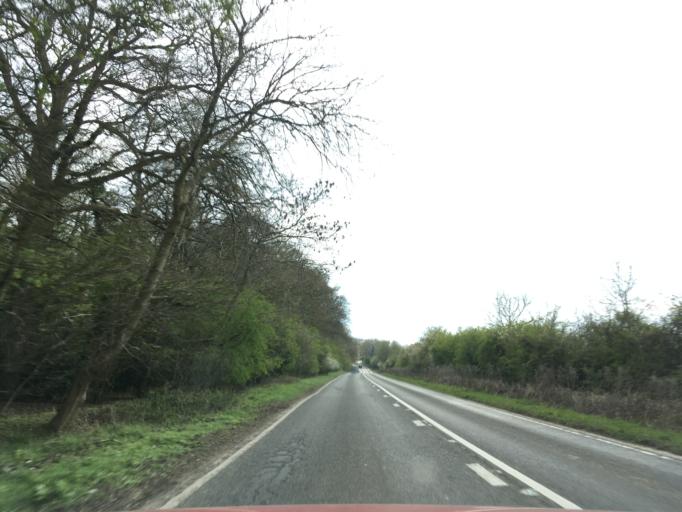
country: GB
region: England
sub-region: Oxfordshire
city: North Leigh
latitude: 51.8096
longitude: -1.4378
